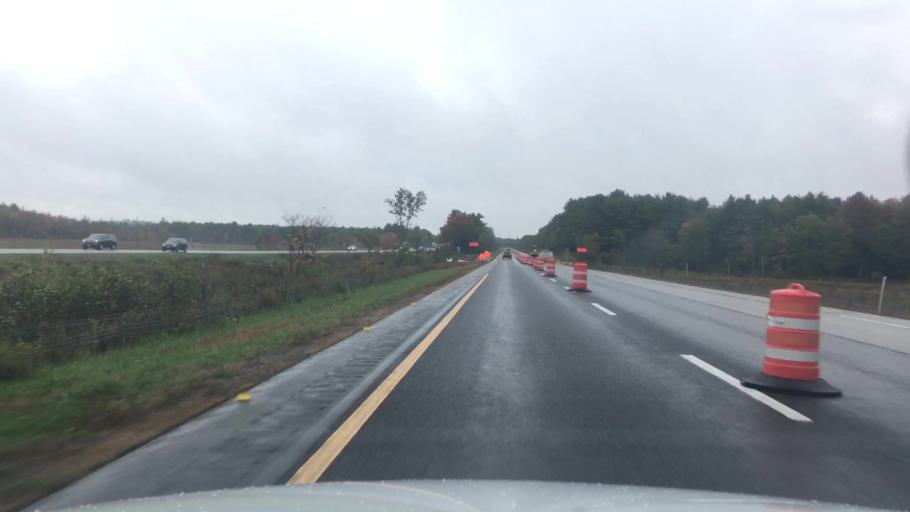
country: US
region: Maine
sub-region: Sagadahoc County
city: Richmond
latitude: 44.1053
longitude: -69.8648
